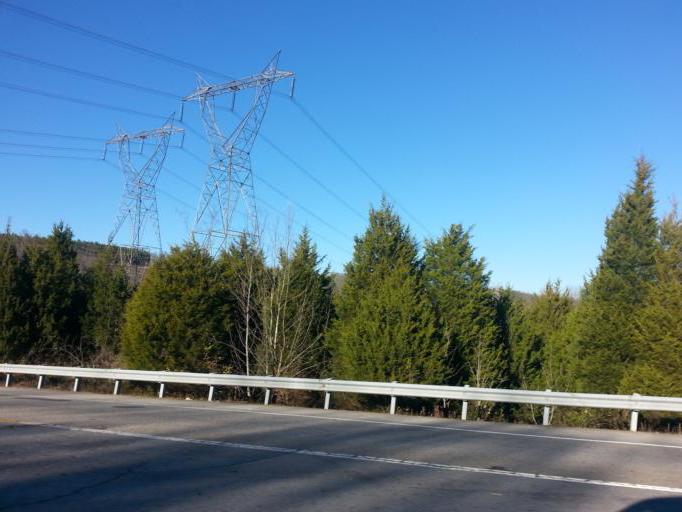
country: US
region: Tennessee
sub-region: Anderson County
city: Oak Ridge
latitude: 35.9921
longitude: -84.1972
